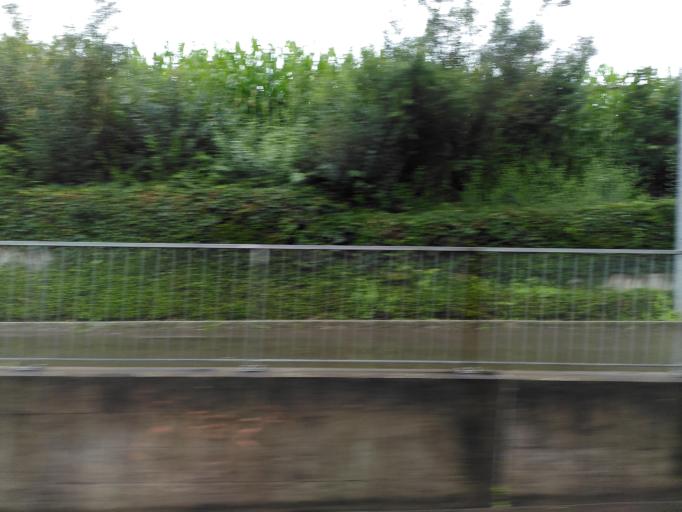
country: CH
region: Schwyz
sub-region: Bezirk Hoefe
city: Freienbach
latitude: 47.2029
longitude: 8.7535
